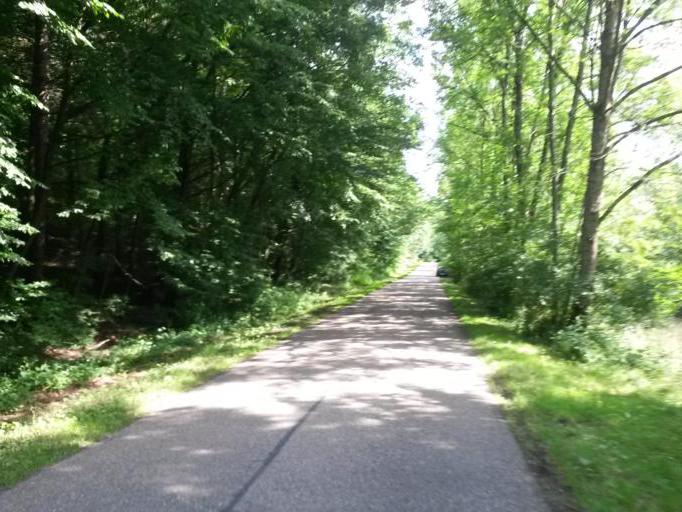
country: DE
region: Baden-Wuerttemberg
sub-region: Karlsruhe Region
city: Konigsbach-Stein
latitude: 48.9131
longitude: 8.5655
